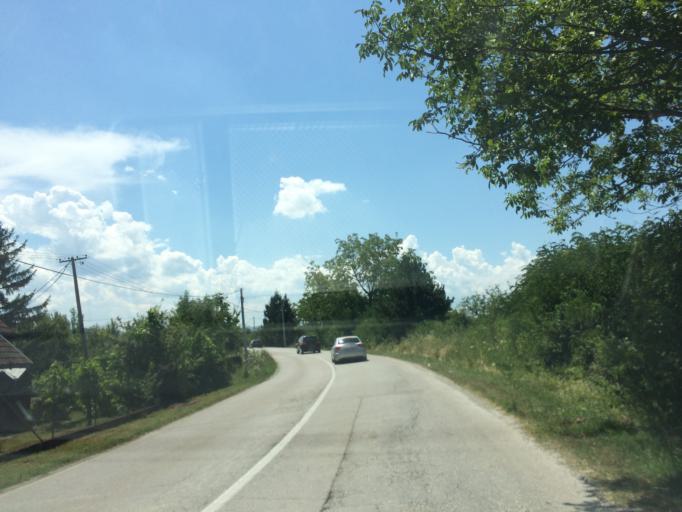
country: RS
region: Central Serbia
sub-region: Kolubarski Okrug
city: Ljig
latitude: 44.2340
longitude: 20.1839
